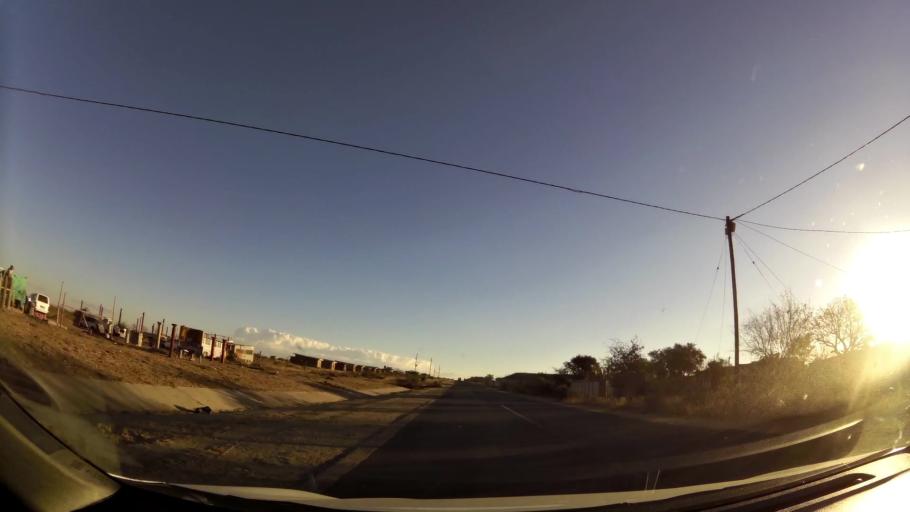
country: ZA
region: Limpopo
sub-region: Capricorn District Municipality
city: Polokwane
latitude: -23.8298
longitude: 29.3753
